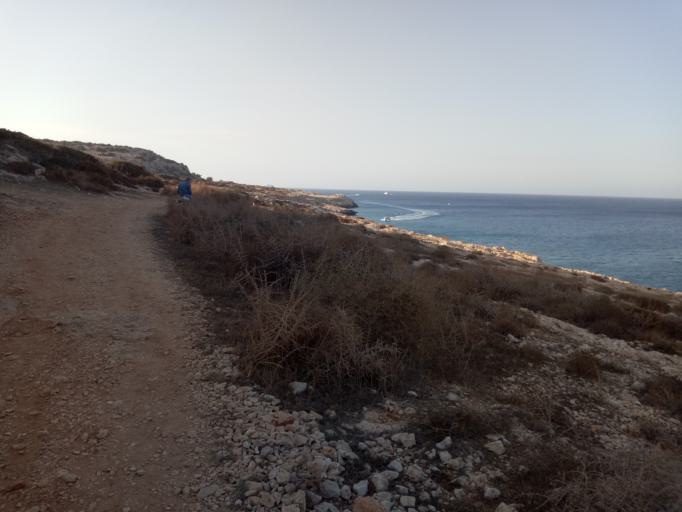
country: CY
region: Ammochostos
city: Protaras
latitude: 34.9695
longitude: 34.0758
